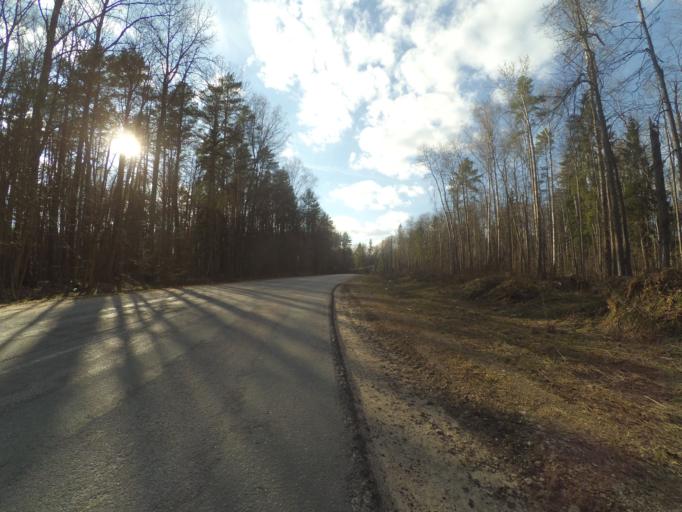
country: RU
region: Moskovskaya
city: Pushchino
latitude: 54.9051
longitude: 37.7287
